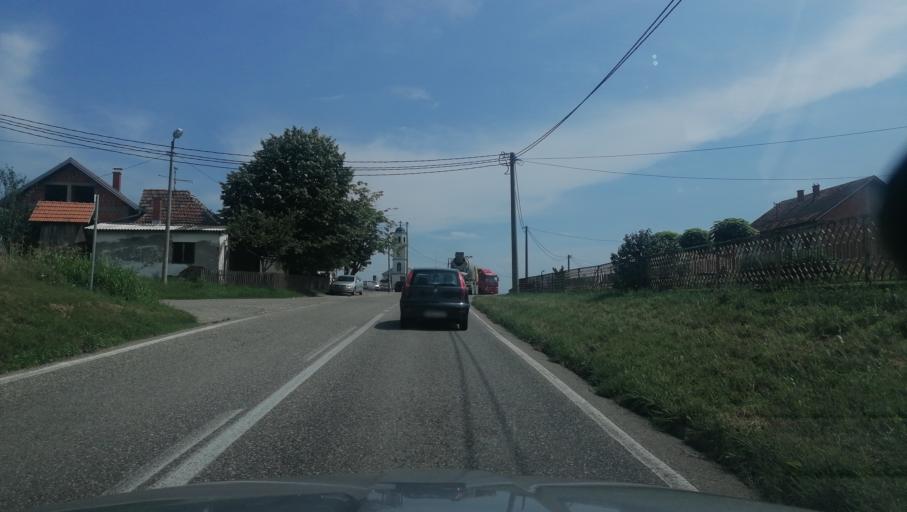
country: BA
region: Republika Srpska
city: Velika Obarska
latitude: 44.8104
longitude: 19.0657
